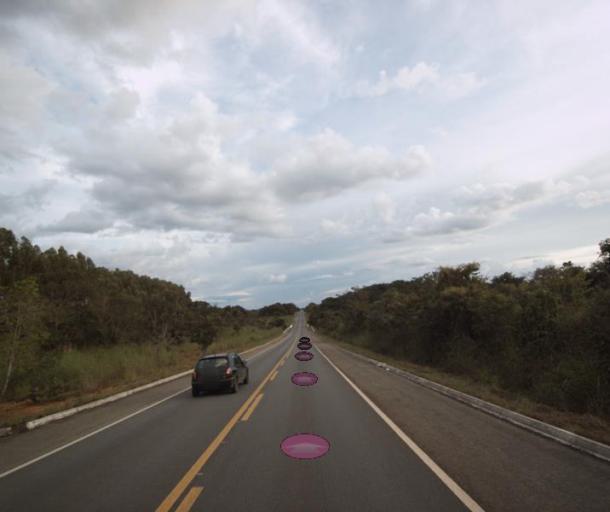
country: BR
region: Goias
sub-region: Barro Alto
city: Barro Alto
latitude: -14.9103
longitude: -48.6463
